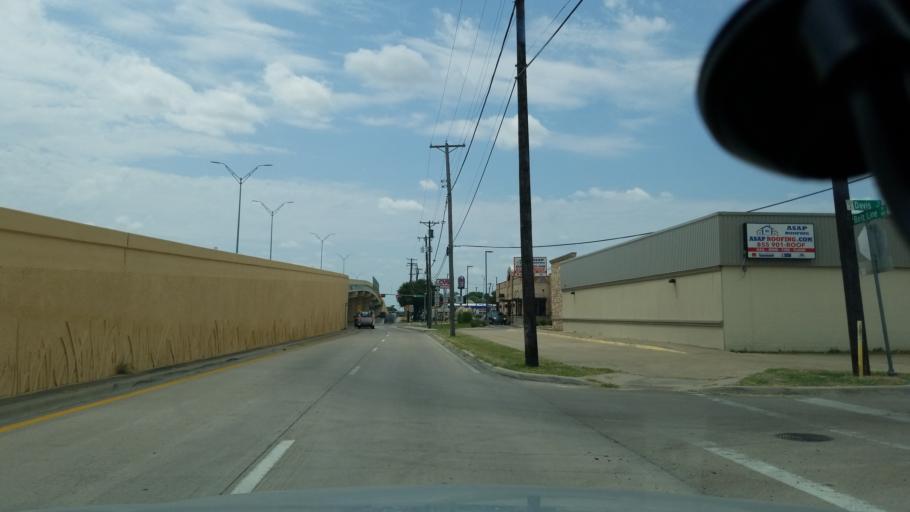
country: US
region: Texas
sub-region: Dallas County
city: Grand Prairie
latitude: 32.7472
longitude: -96.9947
